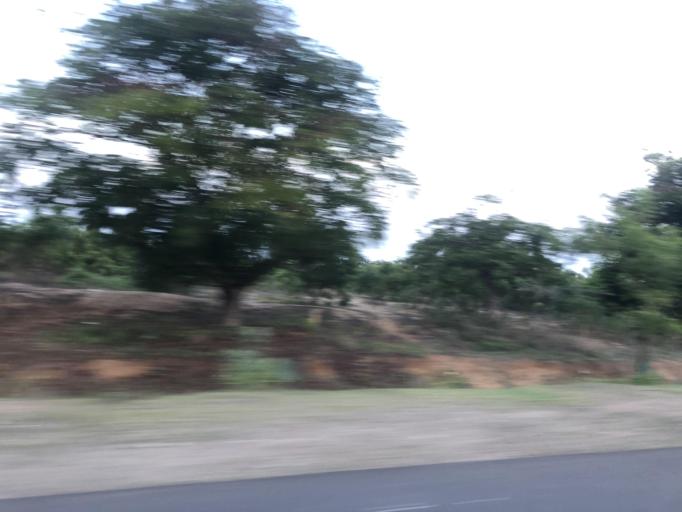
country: IN
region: Tamil Nadu
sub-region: Kancheepuram
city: Mamallapuram
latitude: 12.7587
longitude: 80.2439
